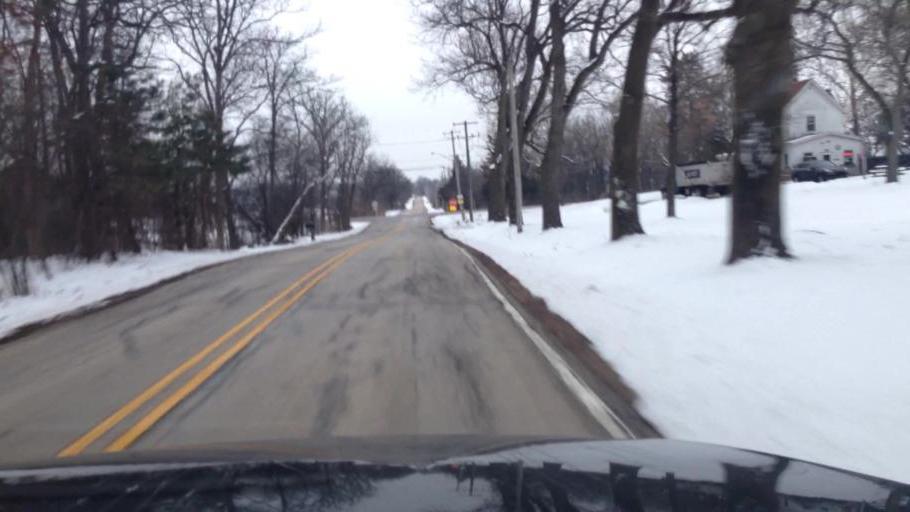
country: US
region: Illinois
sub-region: McHenry County
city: Woodstock
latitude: 42.2562
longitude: -88.4720
